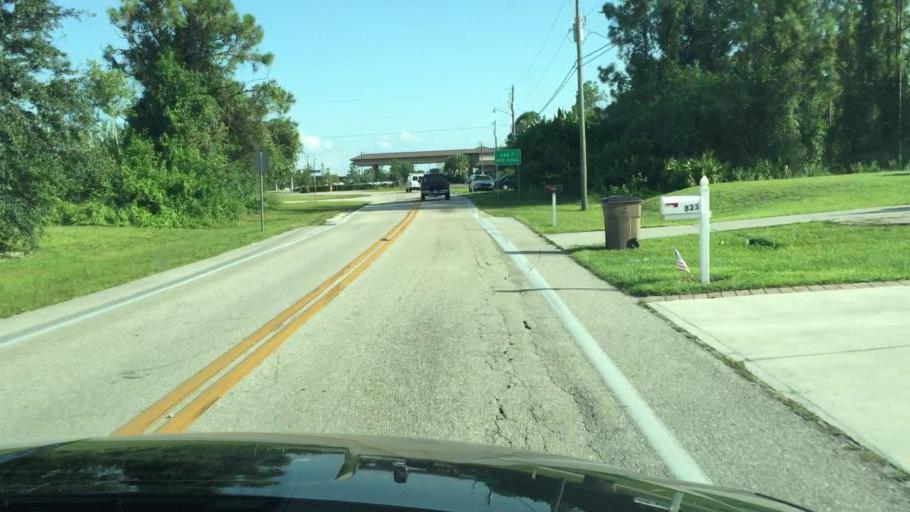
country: US
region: Florida
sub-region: Lee County
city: Gateway
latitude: 26.6236
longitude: -81.7503
